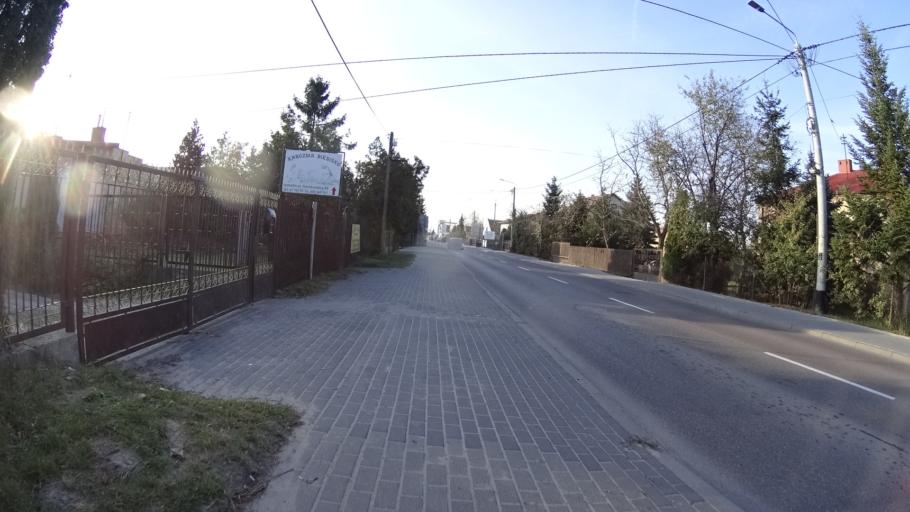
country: PL
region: Masovian Voivodeship
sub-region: Powiat warszawski zachodni
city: Babice
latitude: 52.2877
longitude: 20.8740
